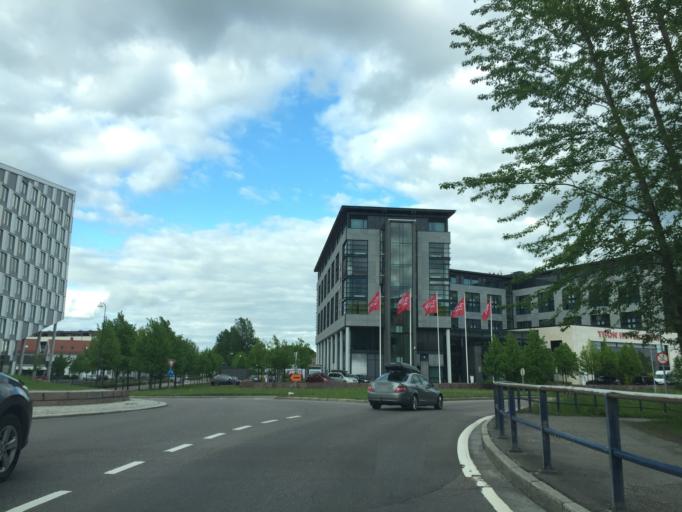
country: NO
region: Akershus
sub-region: Skedsmo
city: Lillestrom
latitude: 59.9505
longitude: 11.0466
